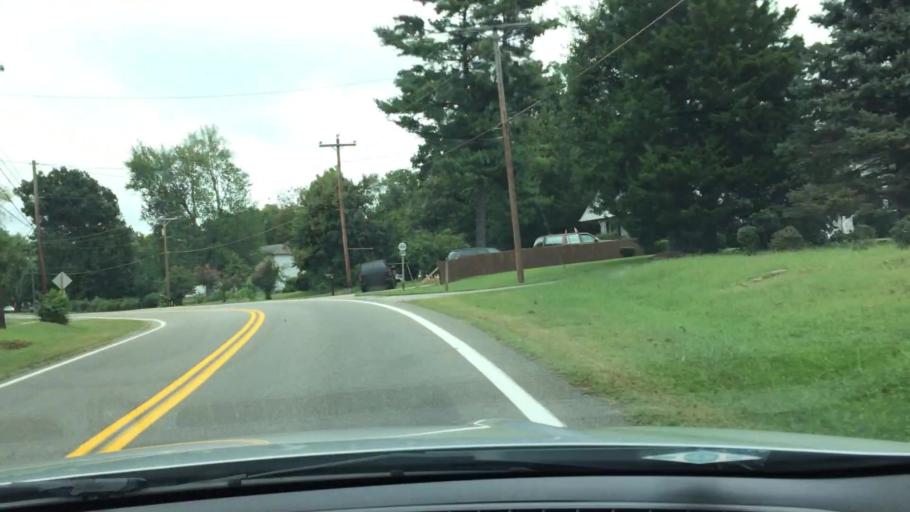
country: US
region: Virginia
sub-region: Pittsylvania County
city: Chatham
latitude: 36.8379
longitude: -79.3929
